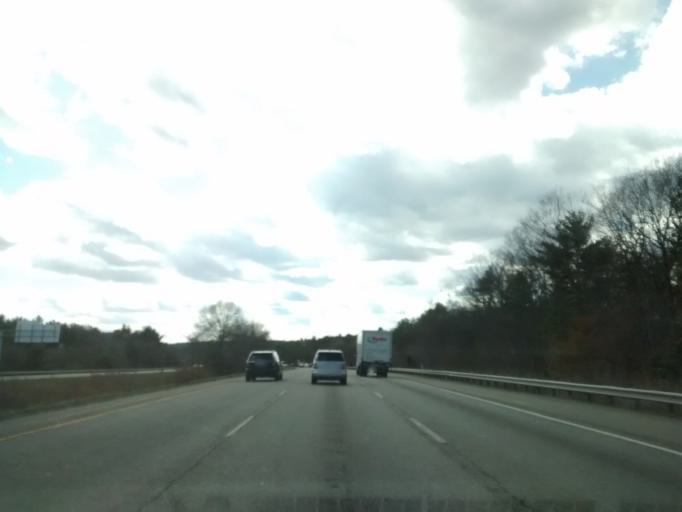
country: US
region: Massachusetts
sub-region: Worcester County
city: Northborough
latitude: 42.3421
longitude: -71.6446
